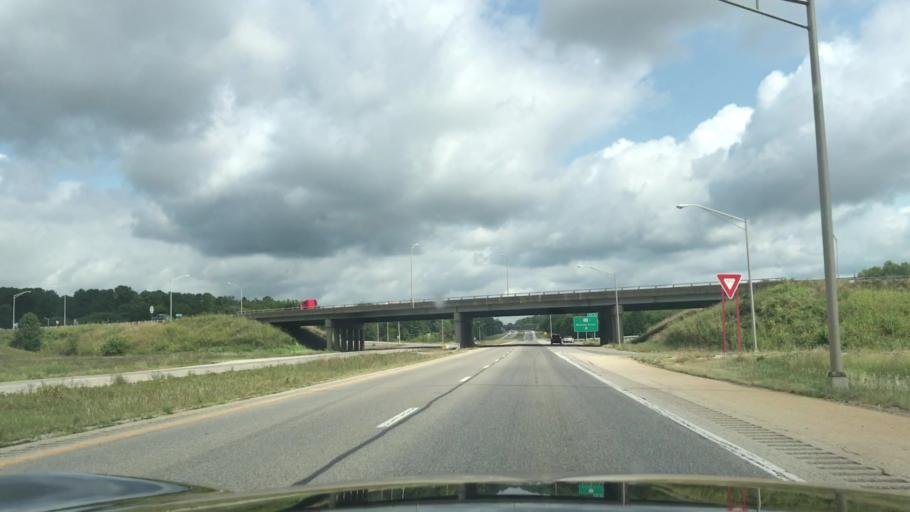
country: US
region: Kentucky
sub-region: Warren County
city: Bowling Green
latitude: 36.9911
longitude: -86.5037
